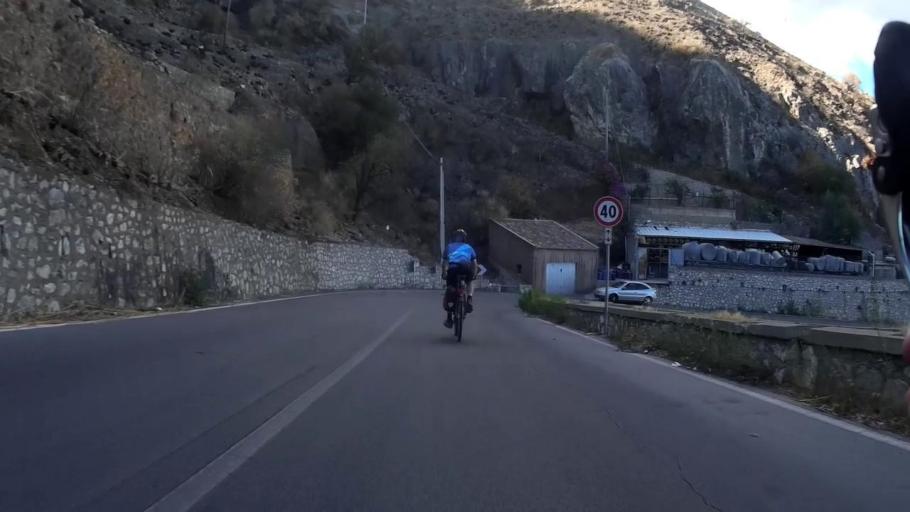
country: IT
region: Sicily
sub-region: Messina
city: Castelmola
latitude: 37.8638
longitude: 15.2763
